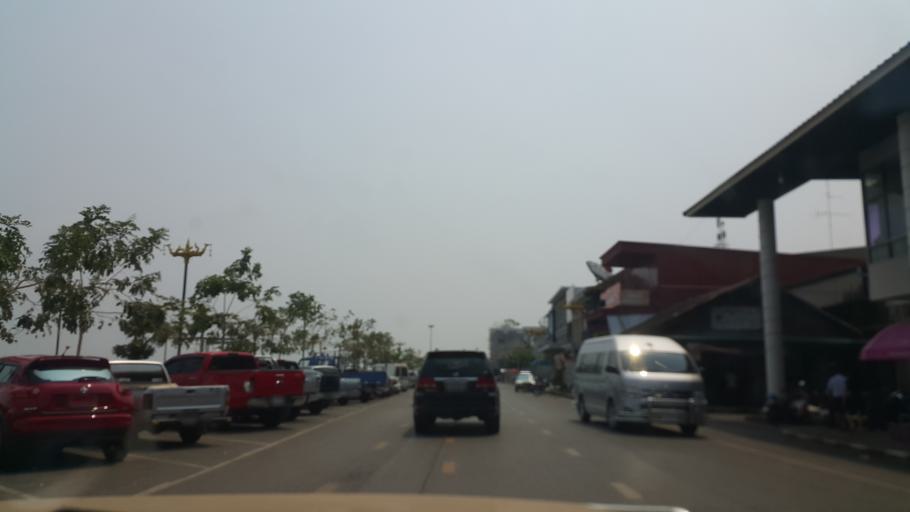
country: TH
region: Nakhon Phanom
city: Nakhon Phanom
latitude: 17.4015
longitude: 104.7891
